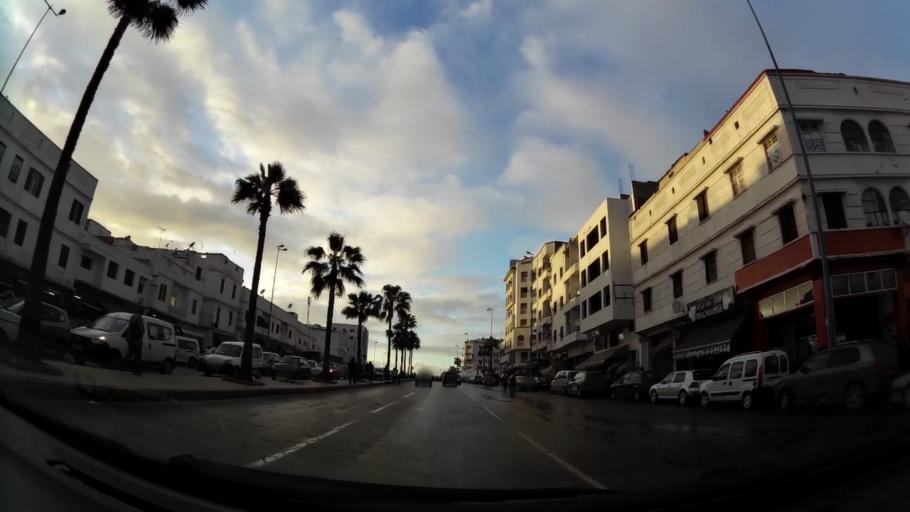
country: MA
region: Grand Casablanca
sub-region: Casablanca
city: Casablanca
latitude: 33.5755
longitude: -7.5989
